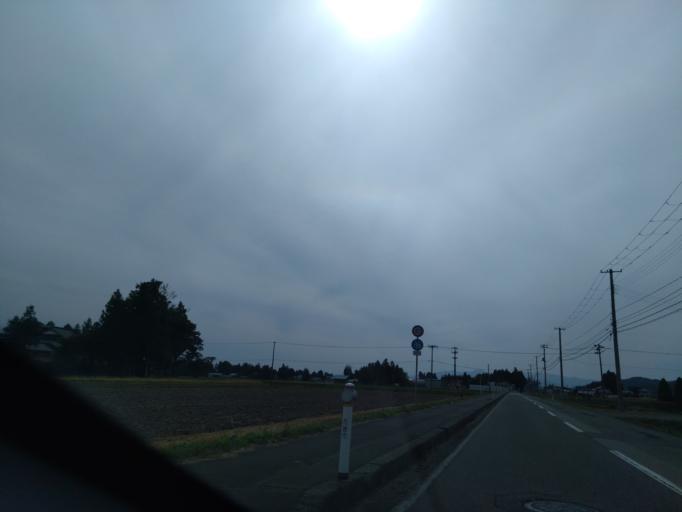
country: JP
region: Iwate
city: Hanamaki
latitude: 39.4417
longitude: 141.0833
